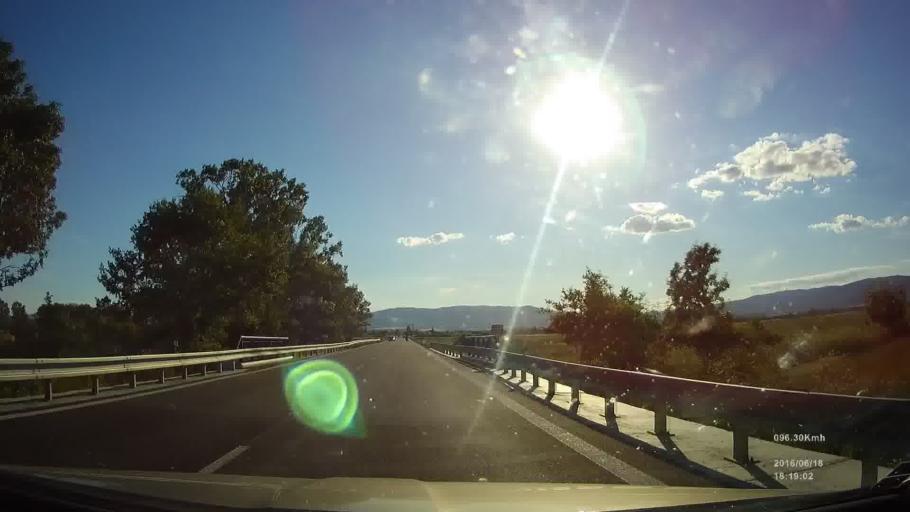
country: SK
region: Kosicky
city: Secovce
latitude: 48.7000
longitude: 21.7287
